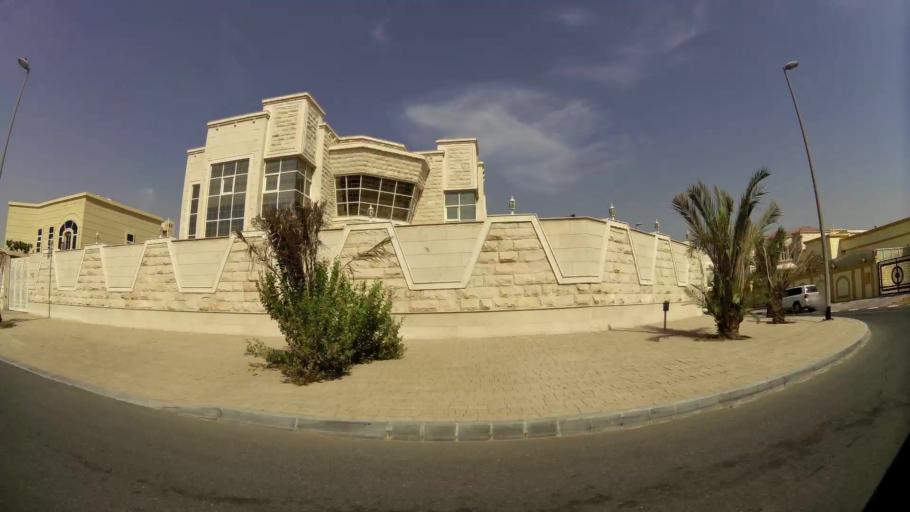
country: AE
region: Ash Shariqah
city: Sharjah
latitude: 25.2073
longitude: 55.4196
